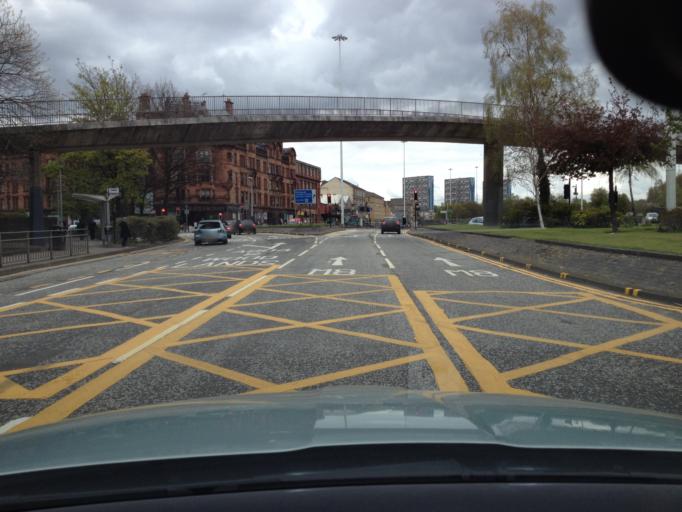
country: GB
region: Scotland
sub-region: Glasgow City
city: Glasgow
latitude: 55.8666
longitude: -4.2715
